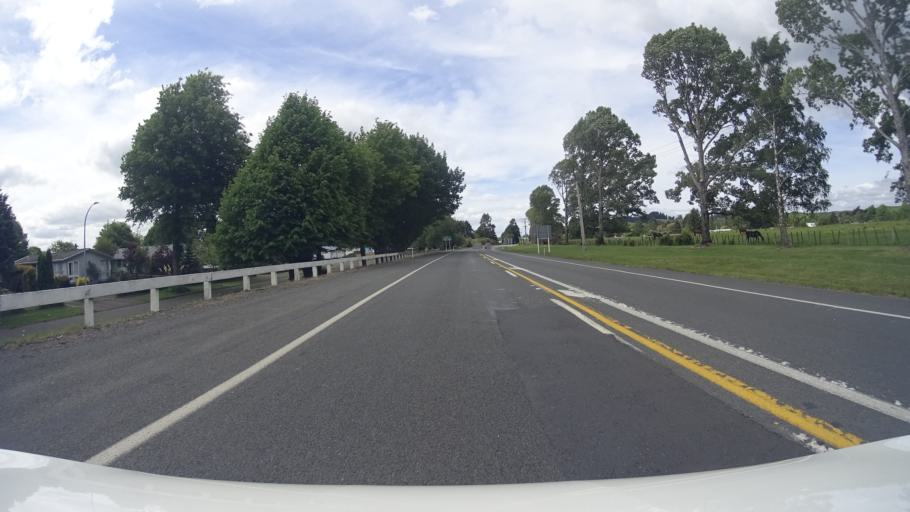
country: NZ
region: Waikato
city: Turangi
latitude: -38.9953
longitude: 175.8056
